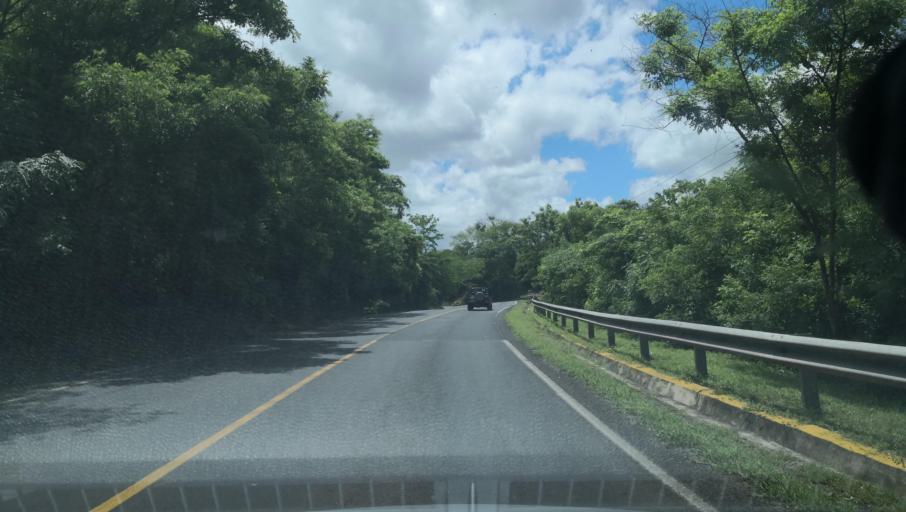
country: NI
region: Esteli
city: Condega
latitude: 13.3121
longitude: -86.3546
